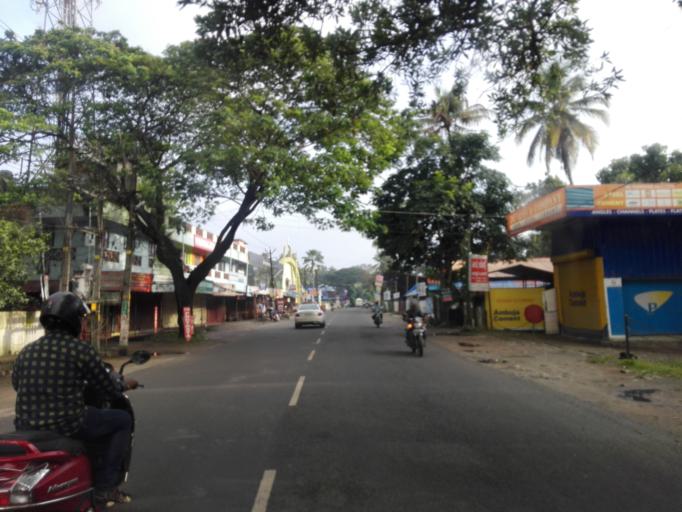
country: IN
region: Kerala
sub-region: Alappuzha
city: Arukutti
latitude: 9.9175
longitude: 76.3625
